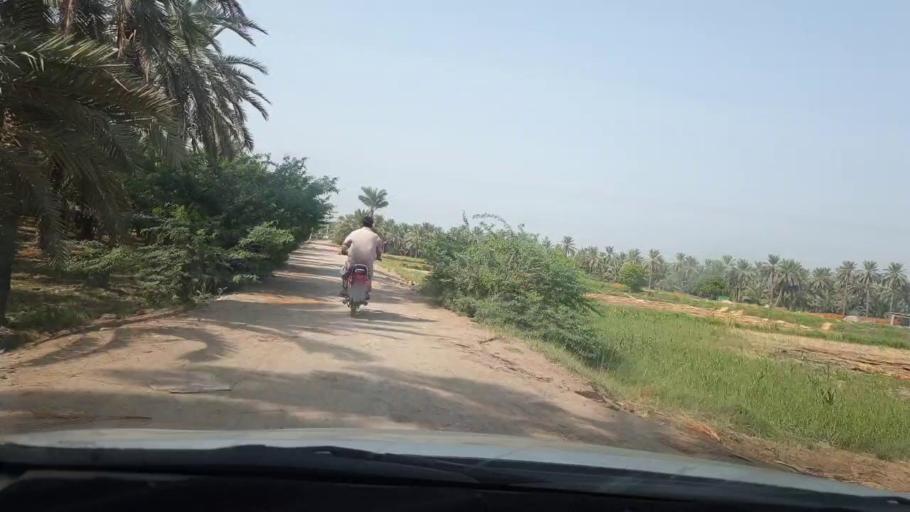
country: PK
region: Sindh
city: Rohri
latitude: 27.5959
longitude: 68.8667
